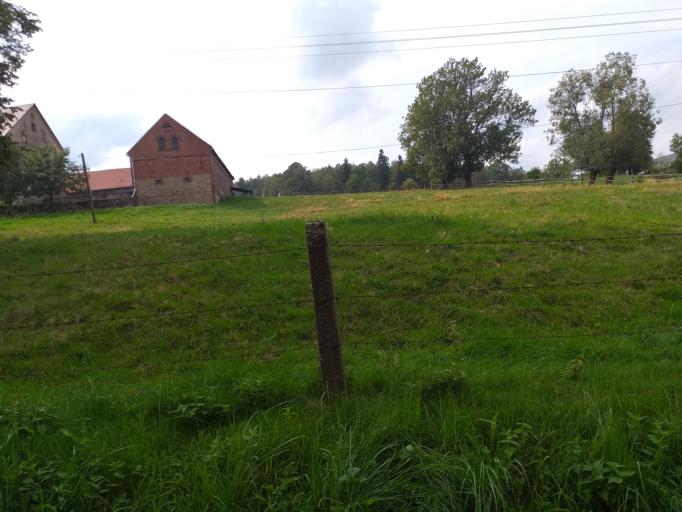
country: PL
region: Lower Silesian Voivodeship
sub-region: Powiat lubanski
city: Lesna
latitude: 51.0049
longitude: 15.3150
